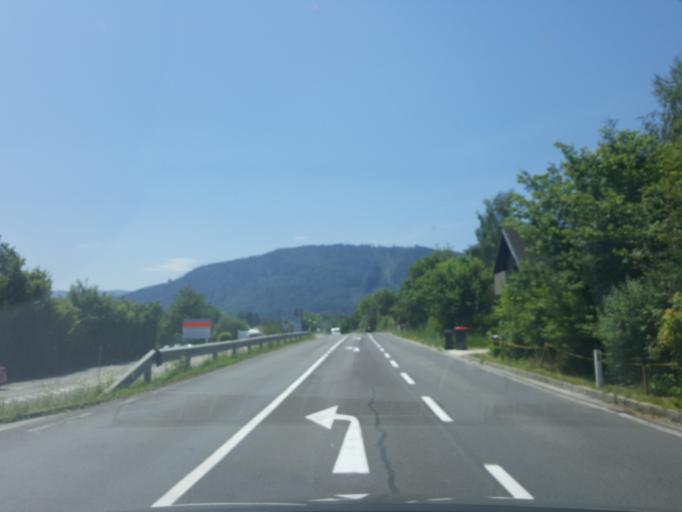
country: AT
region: Upper Austria
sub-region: Politischer Bezirk Vocklabruck
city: Seewalchen
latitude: 47.9393
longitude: 13.5634
